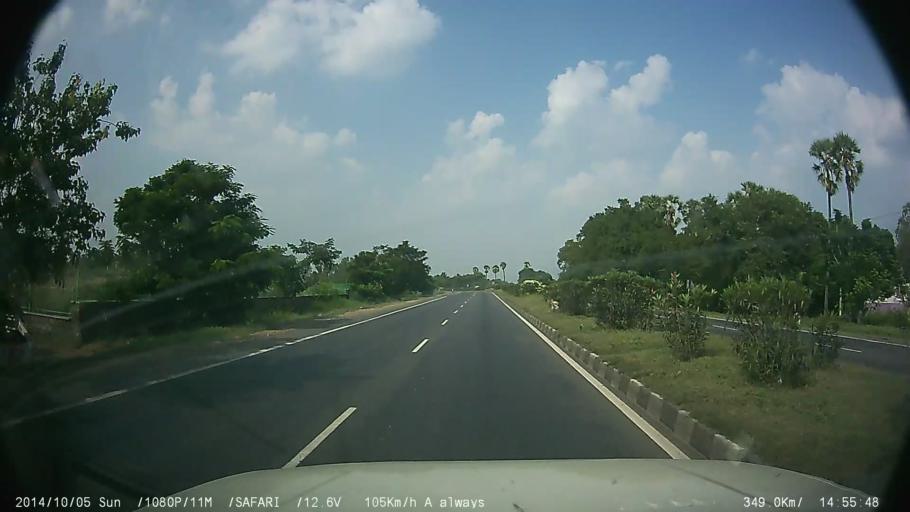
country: IN
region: Tamil Nadu
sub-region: Kancheepuram
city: Madurantakam
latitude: 12.5633
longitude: 79.9131
